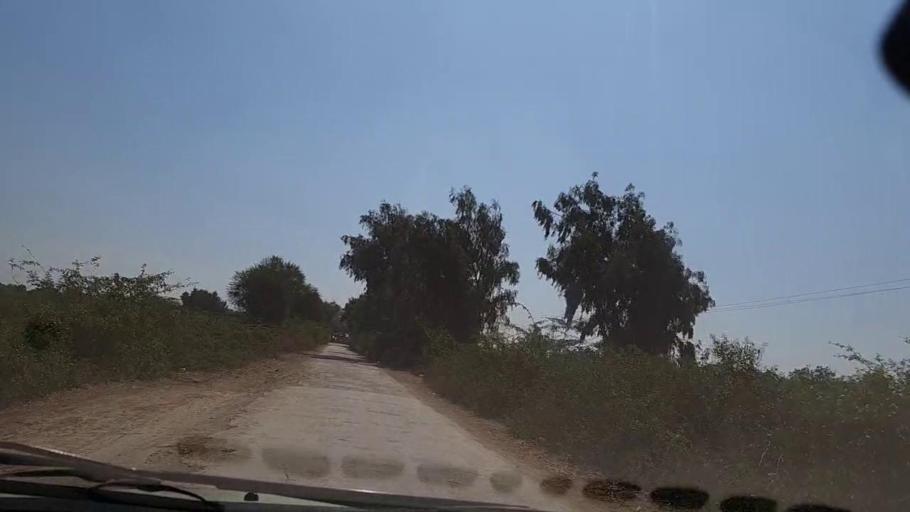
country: PK
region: Sindh
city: Mirpur Khas
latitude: 25.4752
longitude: 69.0493
